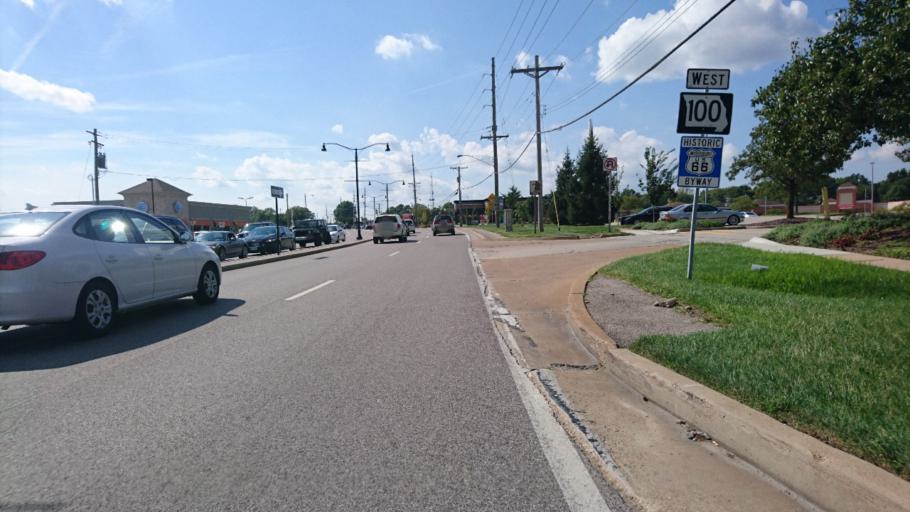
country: US
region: Missouri
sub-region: Saint Louis County
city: Ellisville
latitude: 38.5927
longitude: -90.5865
